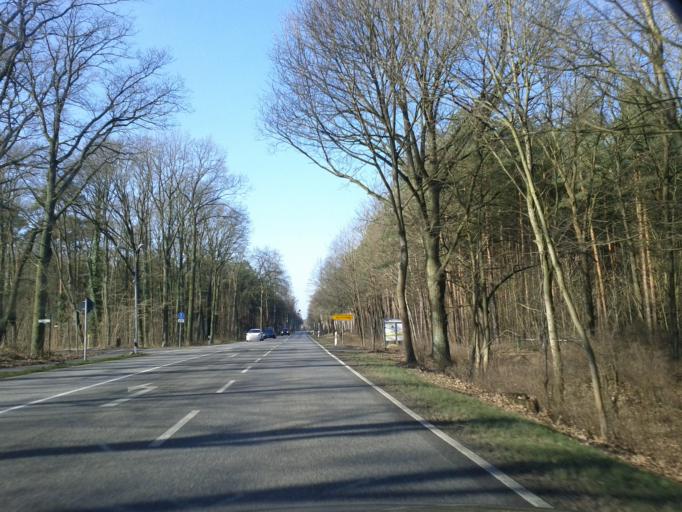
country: DE
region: Brandenburg
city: Spreenhagen
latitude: 52.4006
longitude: 13.9104
